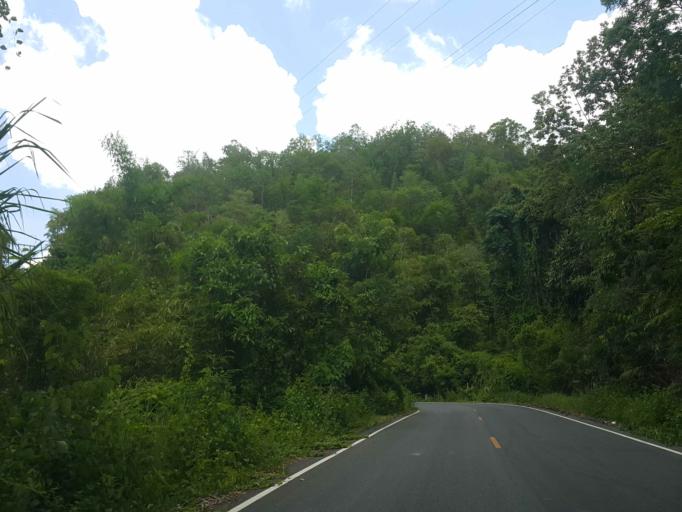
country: TH
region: Nan
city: Wiang Sa
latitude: 18.5343
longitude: 100.5494
